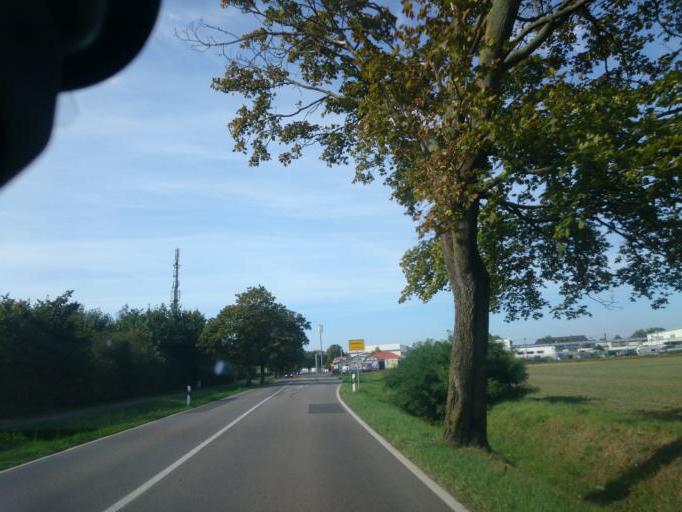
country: DE
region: Mecklenburg-Vorpommern
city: Elmenhorst
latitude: 54.1526
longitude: 12.0212
